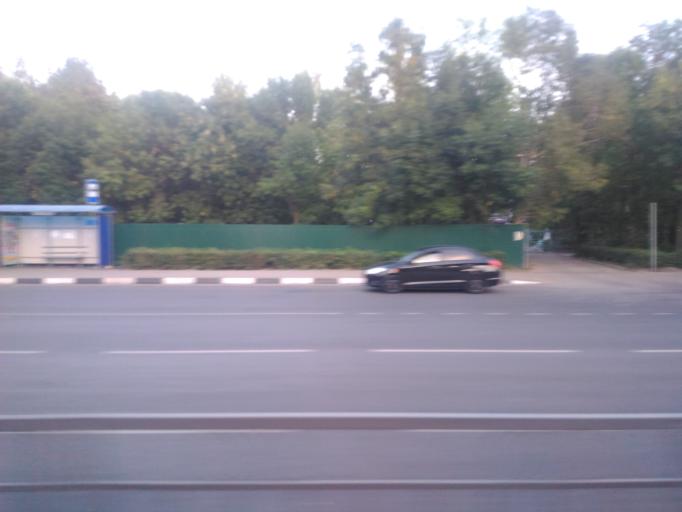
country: RU
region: Ulyanovsk
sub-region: Ulyanovskiy Rayon
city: Ulyanovsk
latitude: 54.2880
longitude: 48.3043
